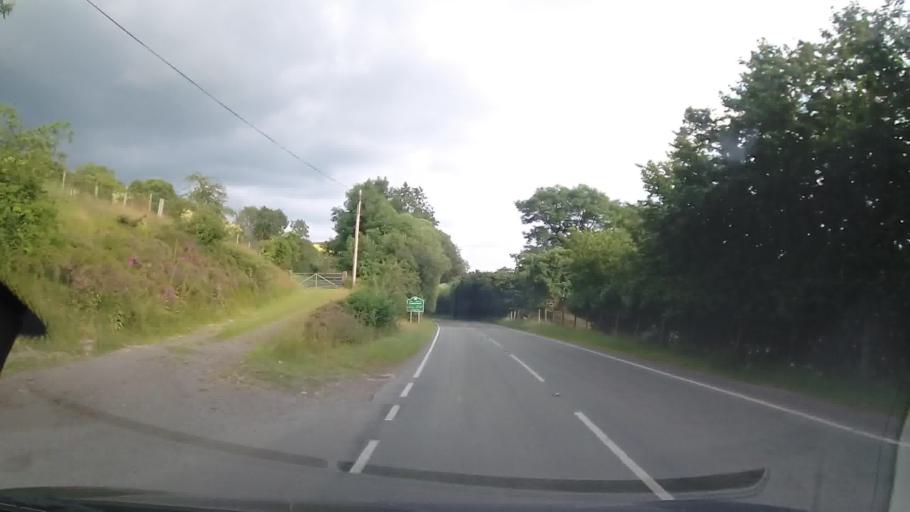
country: GB
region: Wales
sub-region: Sir Powys
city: Llangynog
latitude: 52.8461
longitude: -3.4274
